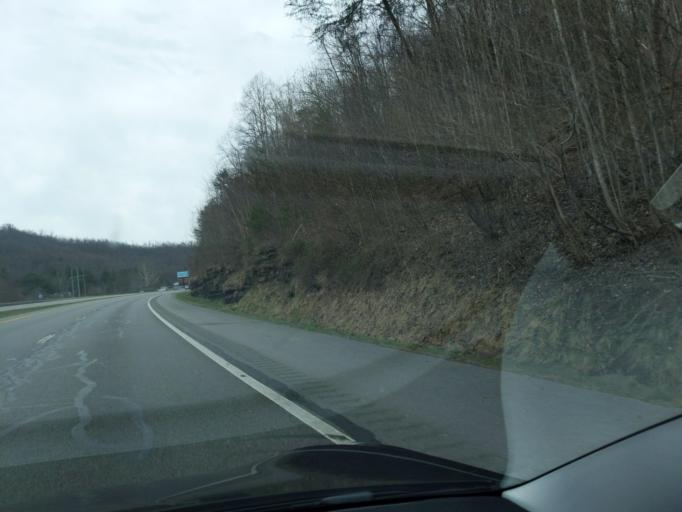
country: US
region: Kentucky
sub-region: Knox County
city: Barbourville
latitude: 36.8763
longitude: -83.8238
